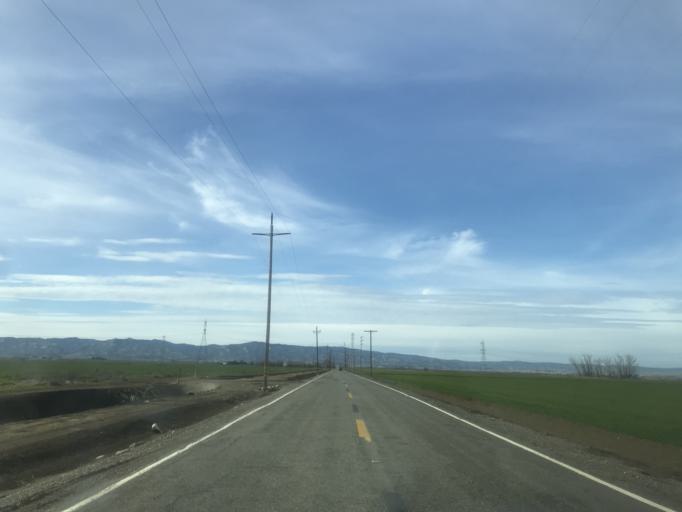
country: US
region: California
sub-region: Yolo County
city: Cottonwood
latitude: 38.6638
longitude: -121.9267
